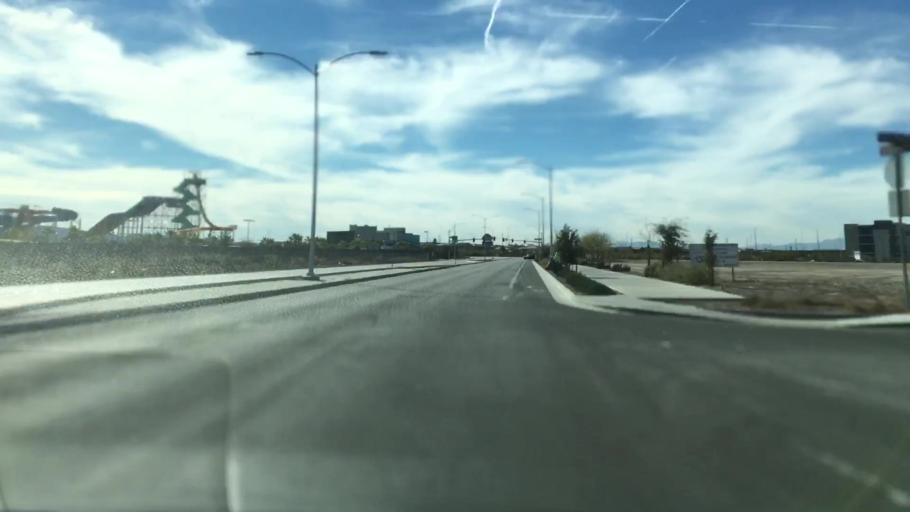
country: US
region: Nevada
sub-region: Clark County
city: Henderson
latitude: 36.0745
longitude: -115.0245
